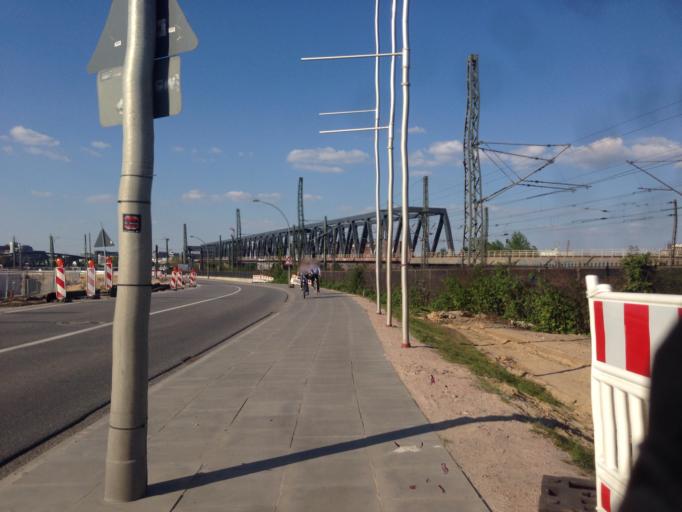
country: DE
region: Hamburg
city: Hammerbrook
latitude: 53.5349
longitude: 10.0241
